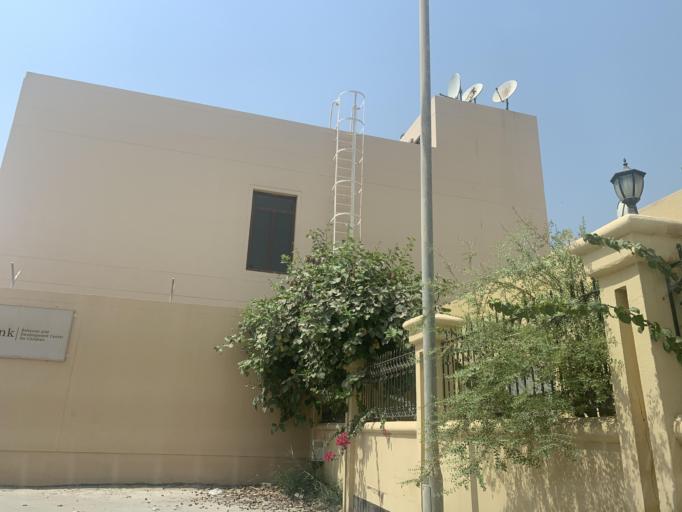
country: BH
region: Manama
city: Jidd Hafs
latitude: 26.1976
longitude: 50.4913
